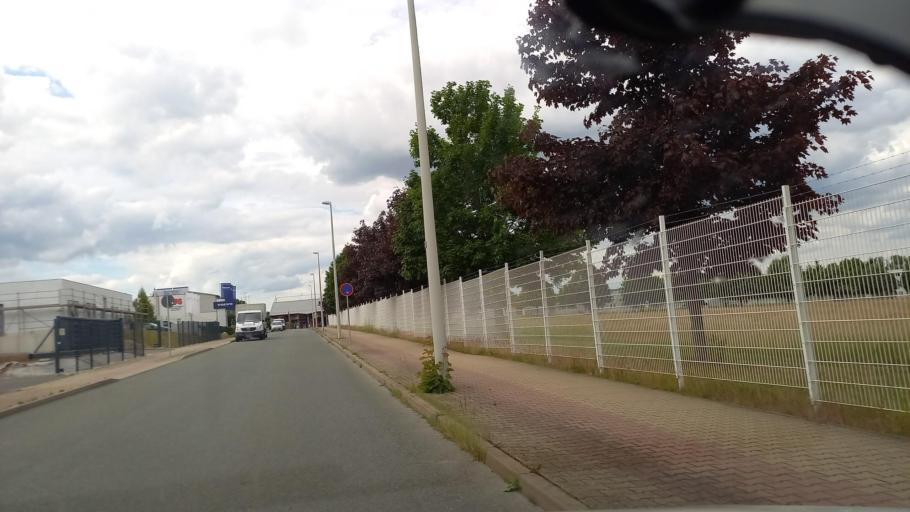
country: DE
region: Saxony
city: Weissenborn
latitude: 50.7270
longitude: 12.4699
